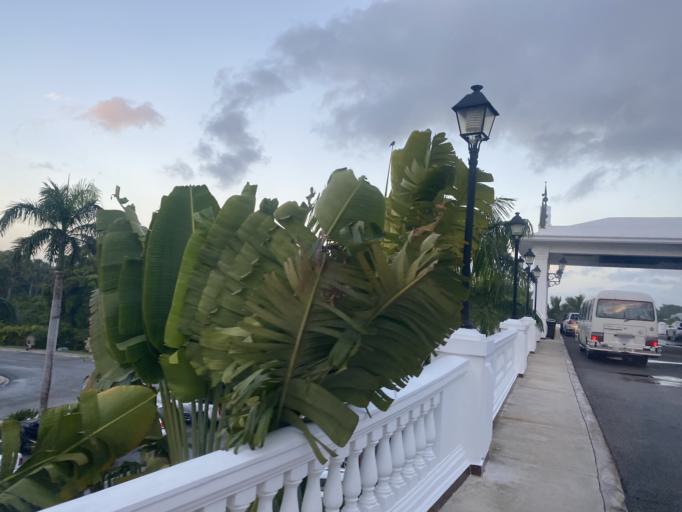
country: DO
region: San Juan
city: Punta Cana
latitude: 18.7222
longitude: -68.4594
